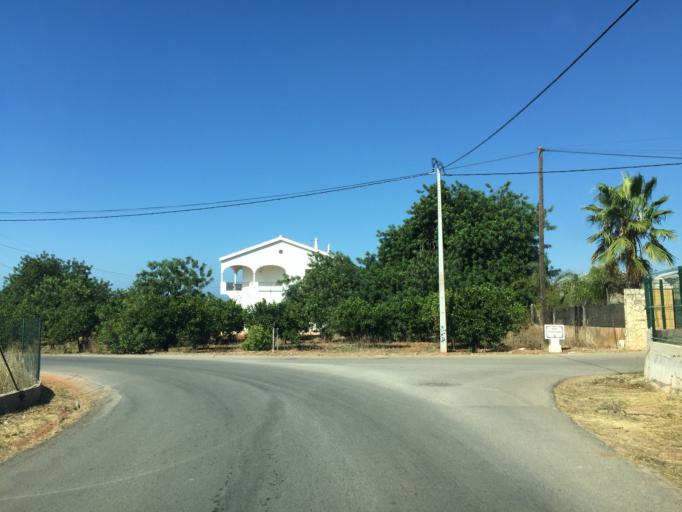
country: PT
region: Faro
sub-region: Loule
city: Vilamoura
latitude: 37.1138
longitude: -8.0858
